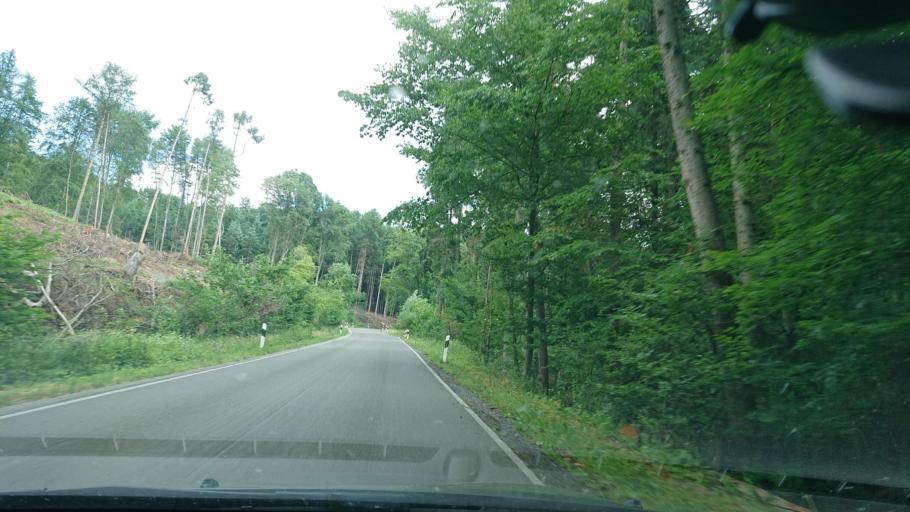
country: DE
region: North Rhine-Westphalia
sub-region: Regierungsbezirk Detmold
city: Rodinghausen
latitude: 52.2626
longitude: 8.4532
